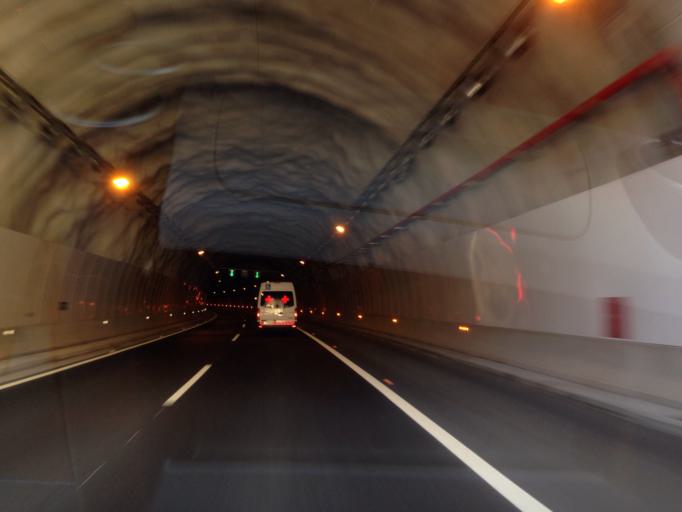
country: ES
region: Canary Islands
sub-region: Provincia de Las Palmas
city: Puerto Rico
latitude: 27.8080
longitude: -15.7126
